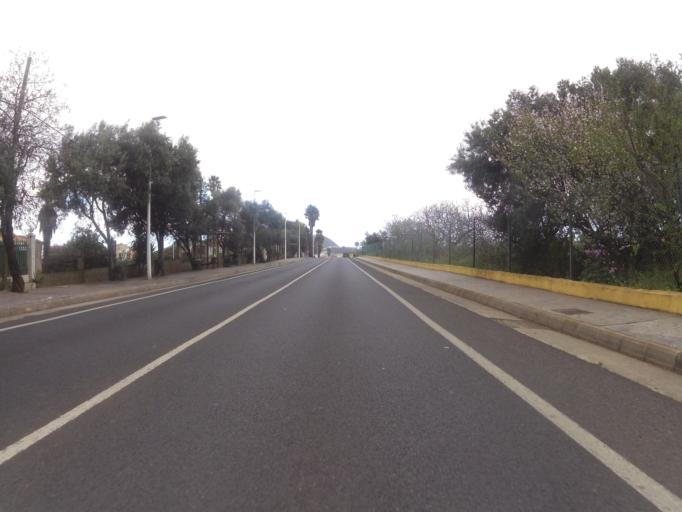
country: ES
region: Canary Islands
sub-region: Provincia de Las Palmas
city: Valsequillo de Gran Canaria
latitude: 27.9920
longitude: -15.4930
